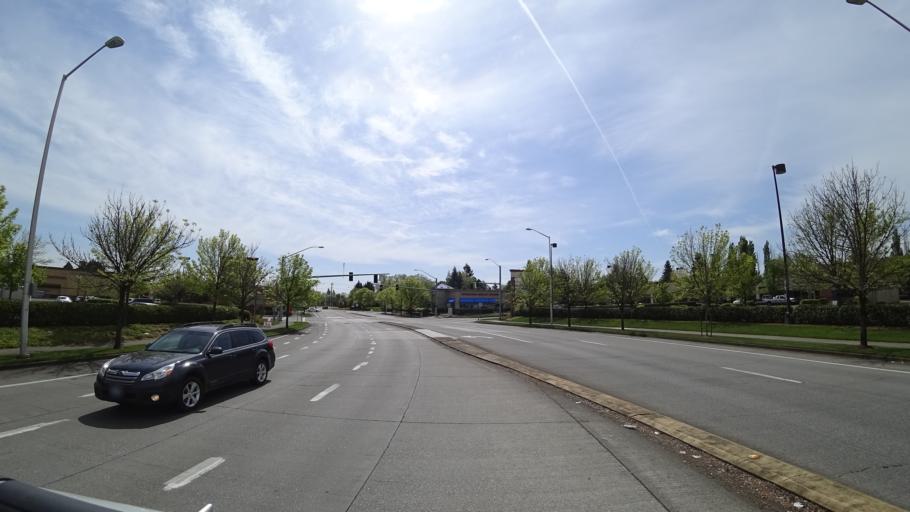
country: US
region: Oregon
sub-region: Washington County
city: Hillsboro
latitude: 45.5299
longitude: -122.9568
